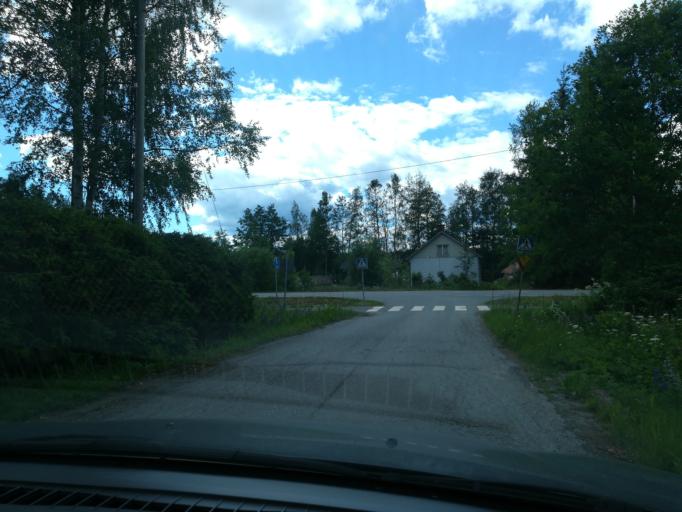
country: FI
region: Southern Savonia
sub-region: Mikkeli
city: Hirvensalmi
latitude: 61.6474
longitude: 26.7725
